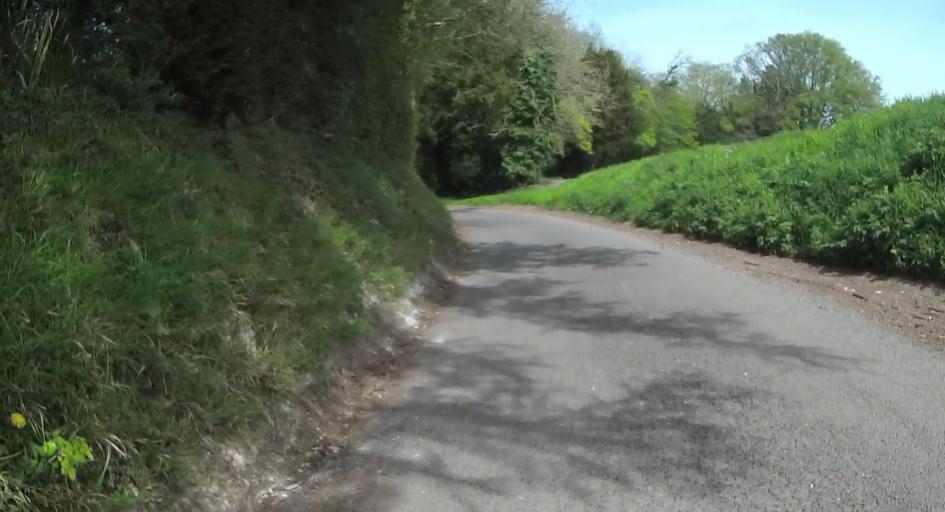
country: GB
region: England
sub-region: Hampshire
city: Chandlers Ford
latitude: 51.0724
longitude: -1.4501
